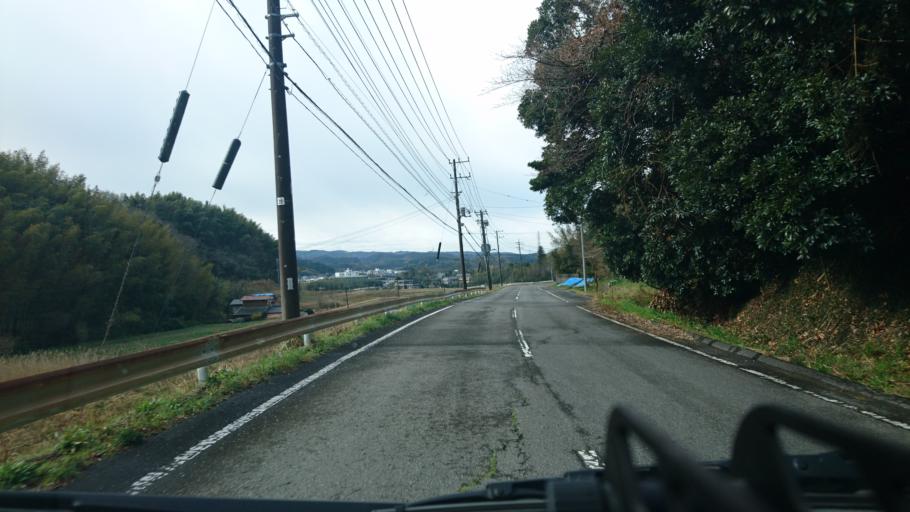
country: JP
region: Chiba
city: Kisarazu
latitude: 35.3155
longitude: 139.9637
